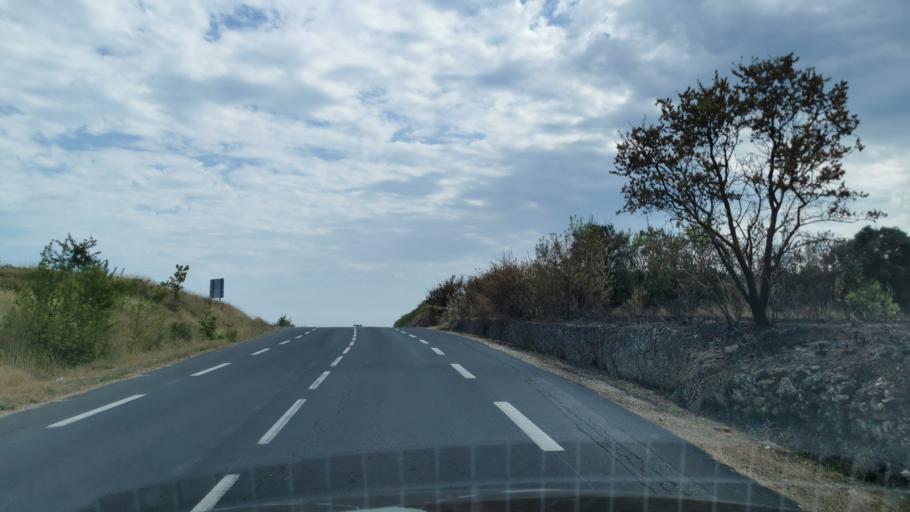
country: FR
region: Languedoc-Roussillon
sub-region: Departement de l'Herault
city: Puisserguier
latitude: 43.3570
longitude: 3.0390
